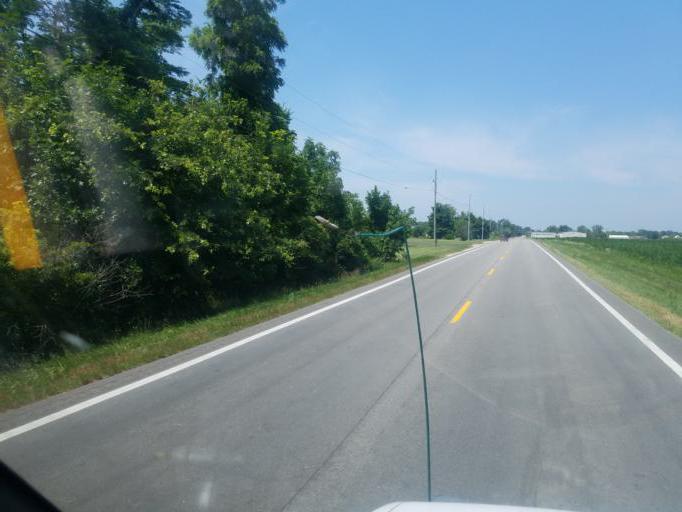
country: US
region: Ohio
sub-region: Auglaize County
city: Saint Marys
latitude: 40.5002
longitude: -84.4346
